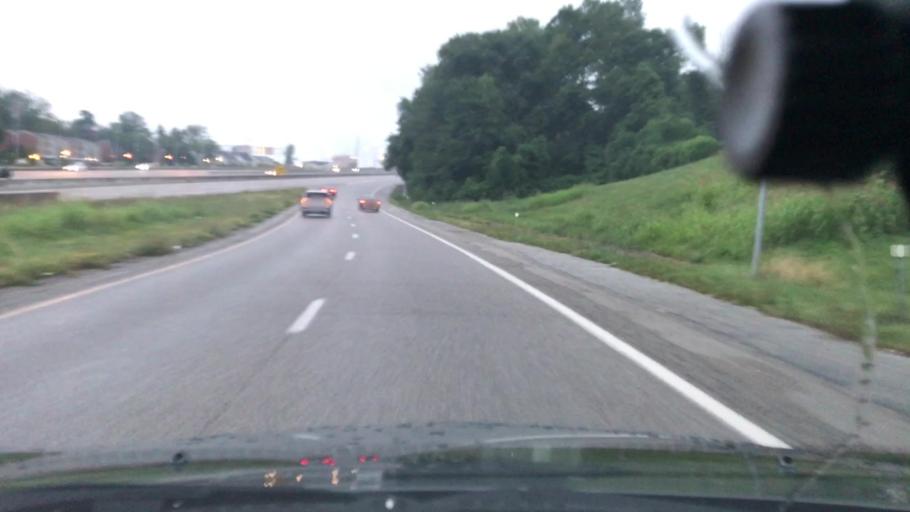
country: US
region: Missouri
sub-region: Saint Louis County
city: Maryland Heights
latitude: 38.6954
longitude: -90.4634
